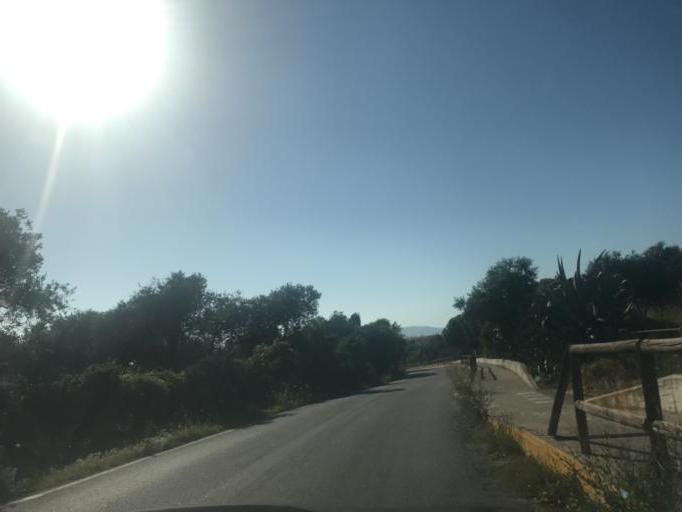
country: IT
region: Sardinia
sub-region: Provincia di Sassari
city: Alghero
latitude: 40.5543
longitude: 8.3332
